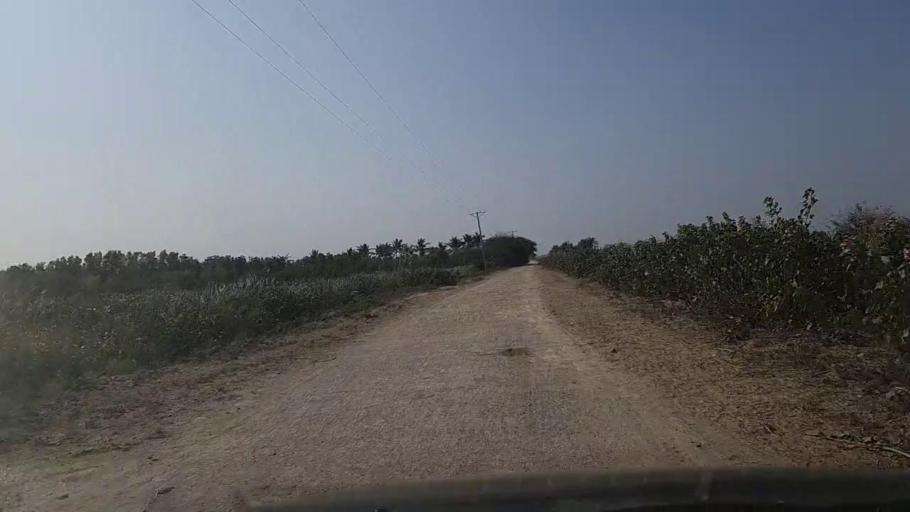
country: PK
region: Sindh
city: Gharo
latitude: 24.6798
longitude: 67.5954
